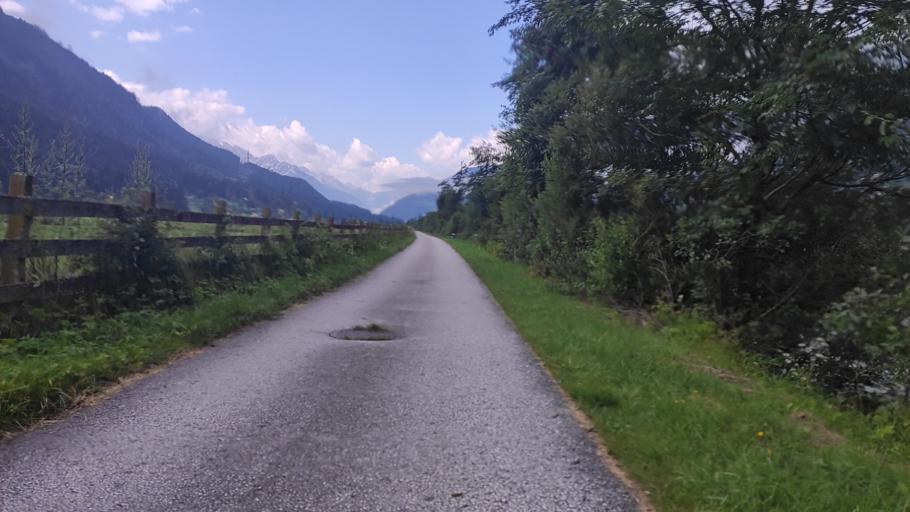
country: AT
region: Salzburg
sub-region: Politischer Bezirk Zell am See
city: Hollersbach im Pinzgau
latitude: 47.2785
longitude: 12.3959
